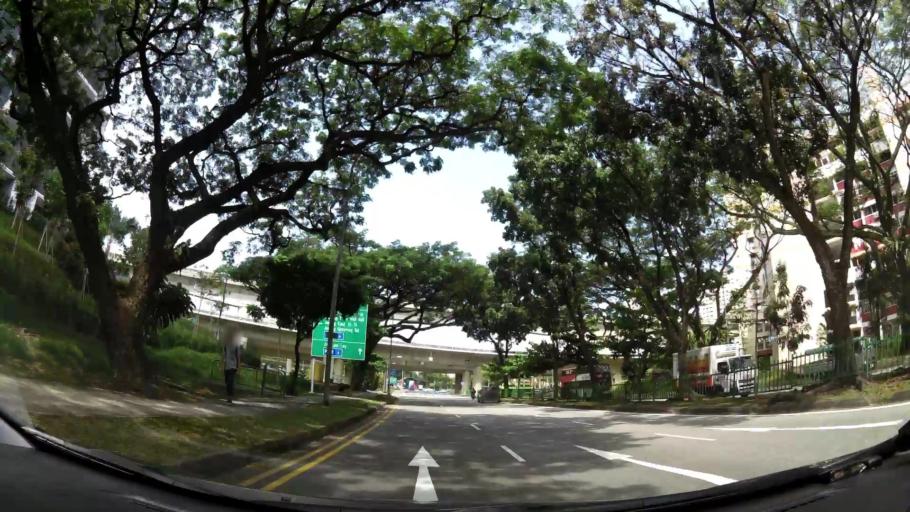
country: SG
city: Singapore
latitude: 1.3367
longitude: 103.7418
